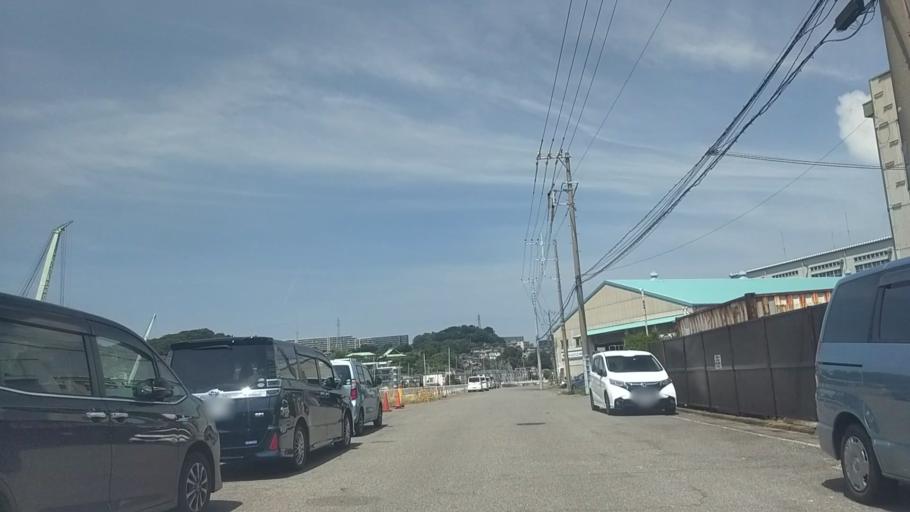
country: JP
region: Kanagawa
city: Yokosuka
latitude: 35.3082
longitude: 139.6414
